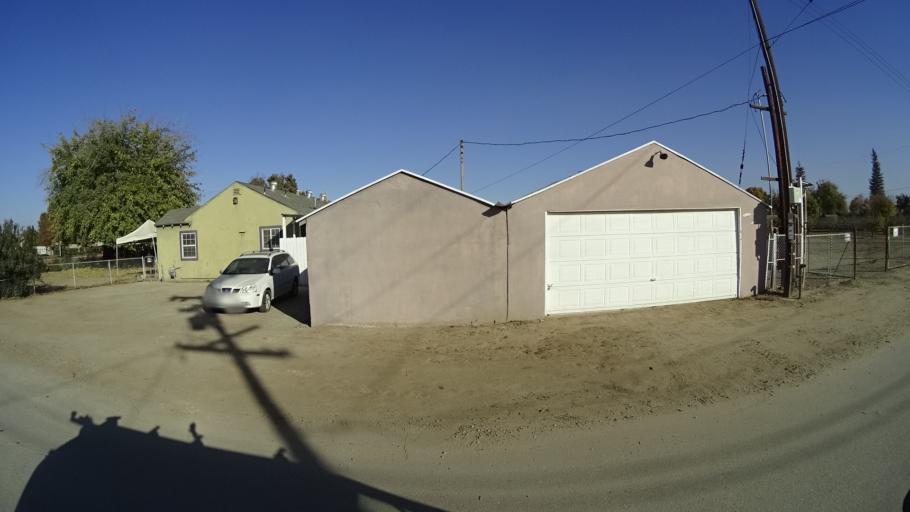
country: US
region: California
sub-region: Kern County
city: Greenfield
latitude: 35.2705
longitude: -119.0385
